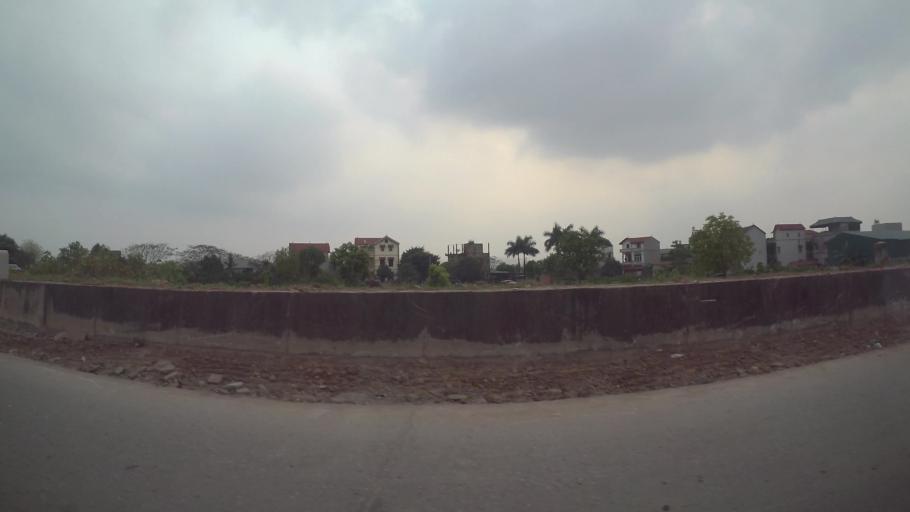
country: VN
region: Ha Noi
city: Trau Quy
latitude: 21.0094
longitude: 105.9054
